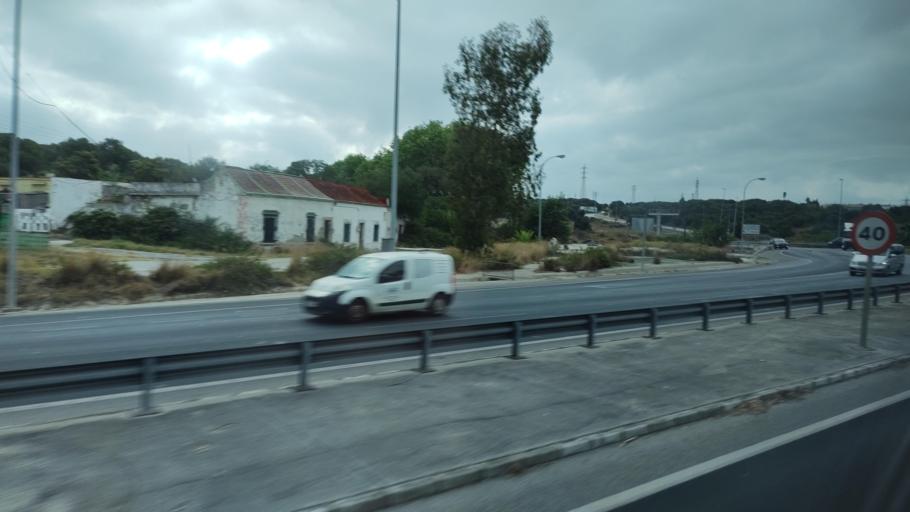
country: ES
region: Andalusia
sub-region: Provincia de Cadiz
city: San Roque
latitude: 36.1831
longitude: -5.3814
